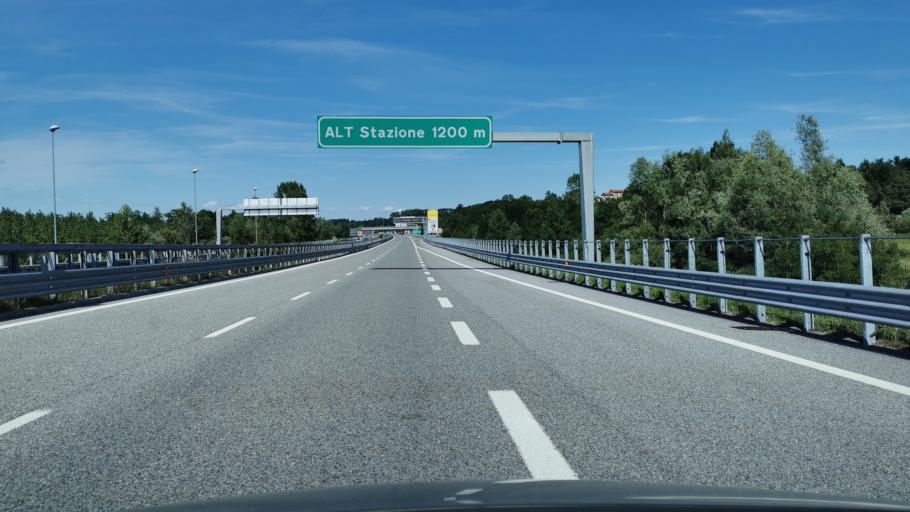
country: IT
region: Piedmont
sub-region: Provincia di Cuneo
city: Castelletto Stura
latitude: 44.4255
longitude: 7.5955
